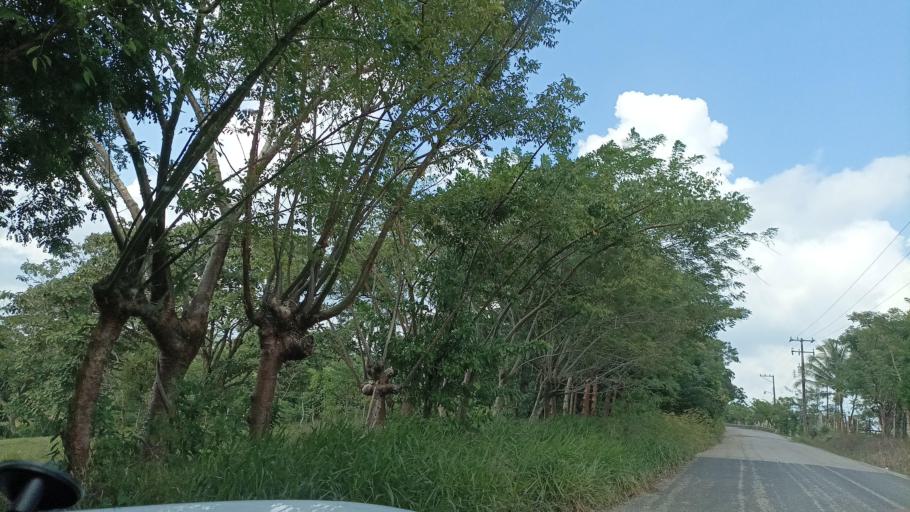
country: MX
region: Veracruz
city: Las Choapas
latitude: 17.7469
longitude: -94.1098
